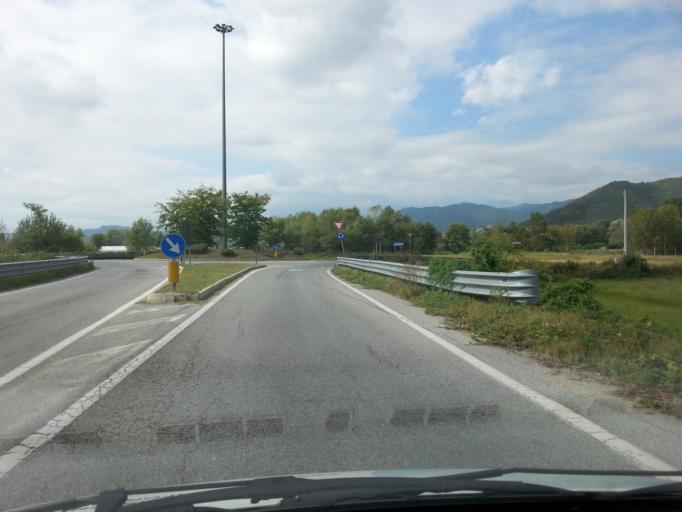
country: IT
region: Piedmont
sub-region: Provincia di Torino
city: Cumiana
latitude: 44.9477
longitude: 7.3886
